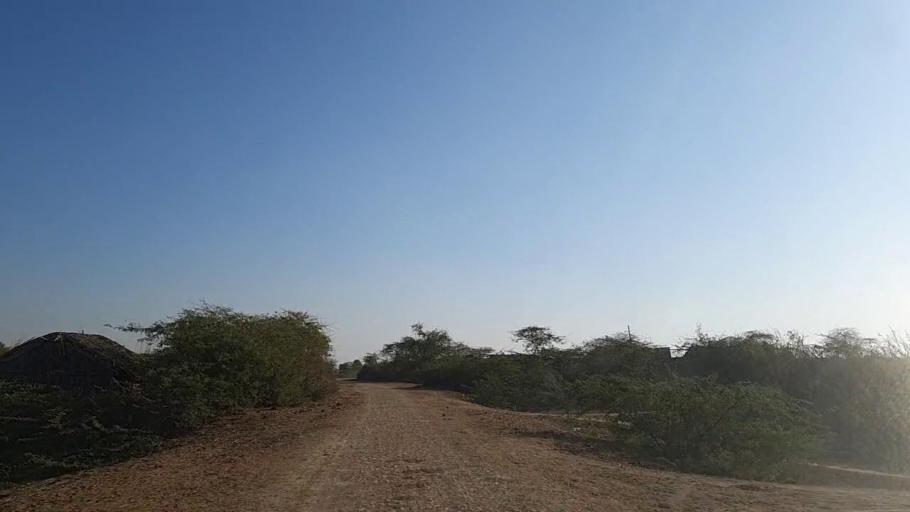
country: PK
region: Sindh
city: Samaro
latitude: 25.3541
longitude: 69.3774
